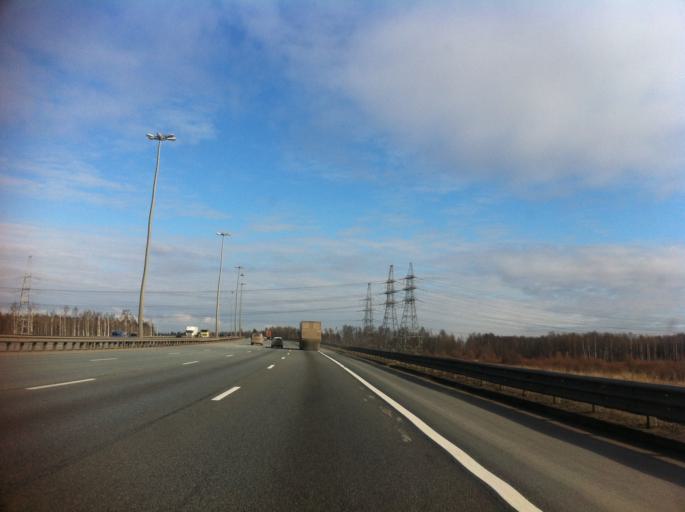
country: RU
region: St.-Petersburg
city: Krasnogvargeisky
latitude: 59.9269
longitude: 30.5328
